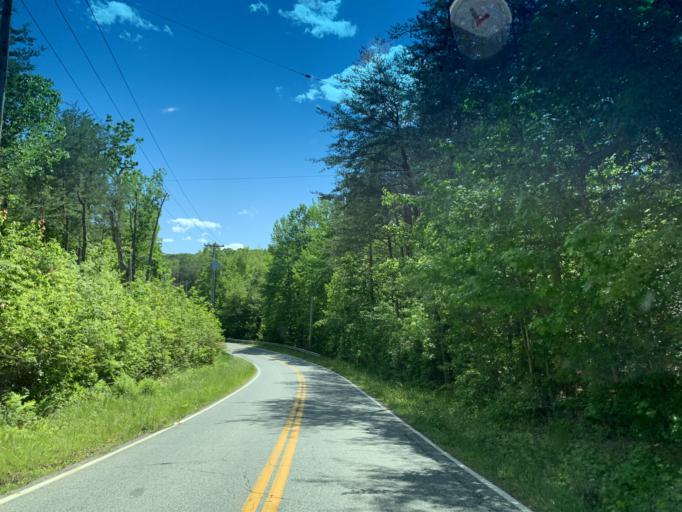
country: US
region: Maryland
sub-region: Cecil County
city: Charlestown
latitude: 39.5350
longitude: -75.9296
